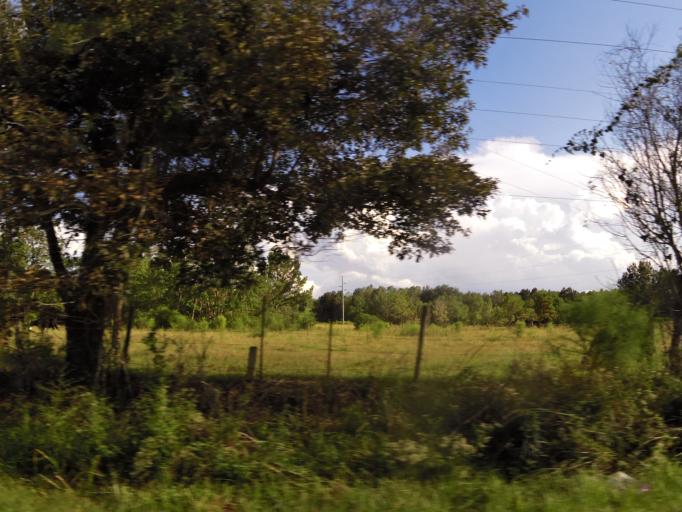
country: US
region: Georgia
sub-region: Brooks County
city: Quitman
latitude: 30.7831
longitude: -83.5877
